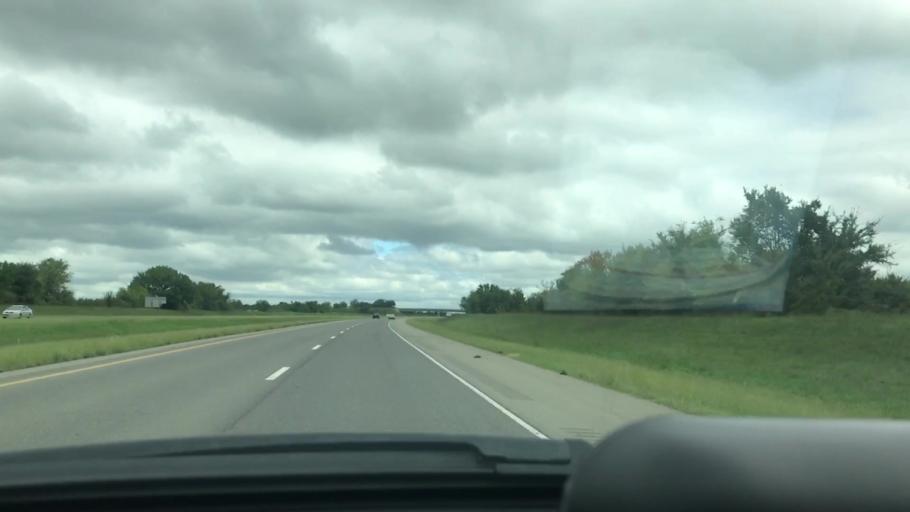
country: US
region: Oklahoma
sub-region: McIntosh County
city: Checotah
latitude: 35.5885
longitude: -95.4885
